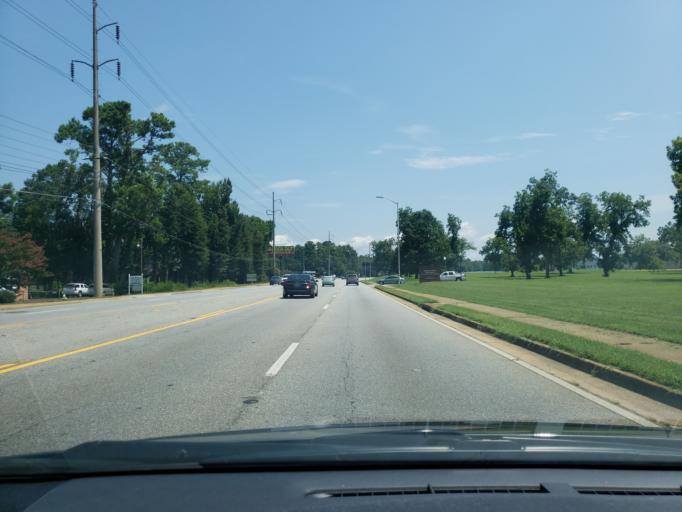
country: US
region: Georgia
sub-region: Dougherty County
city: Albany
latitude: 31.5857
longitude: -84.2112
